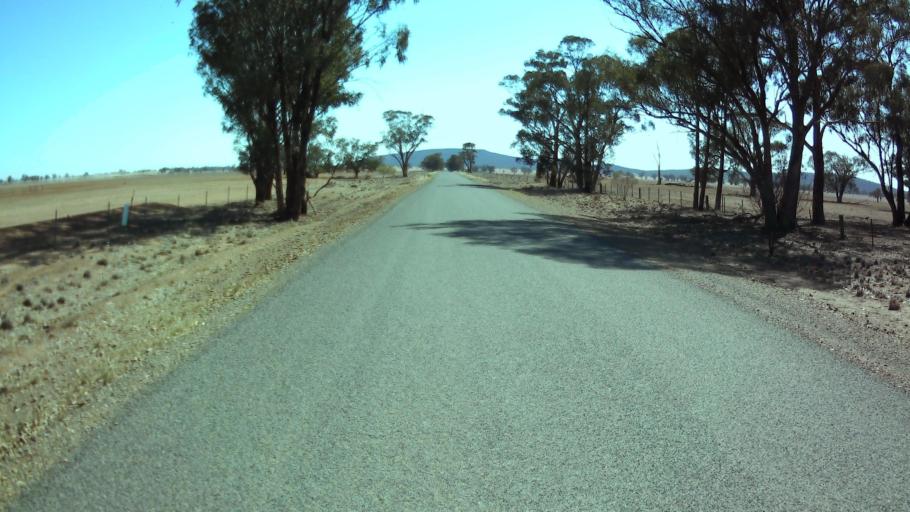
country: AU
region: New South Wales
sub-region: Weddin
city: Grenfell
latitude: -33.7144
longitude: 147.9073
